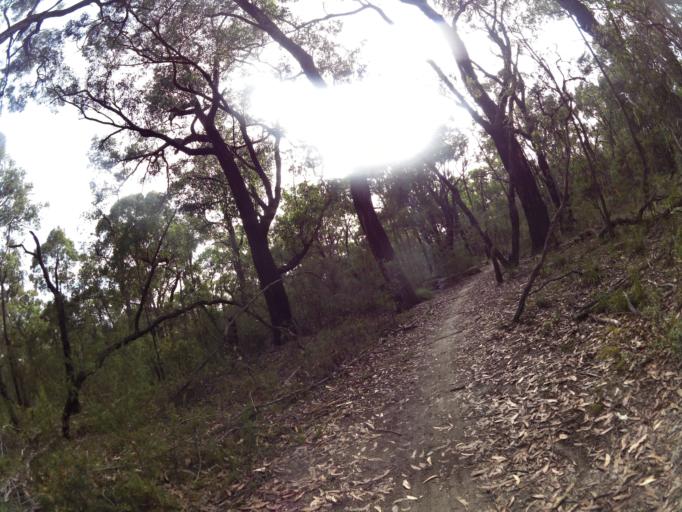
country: AU
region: Victoria
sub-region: Colac-Otway
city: Colac
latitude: -38.4921
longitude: 143.7003
